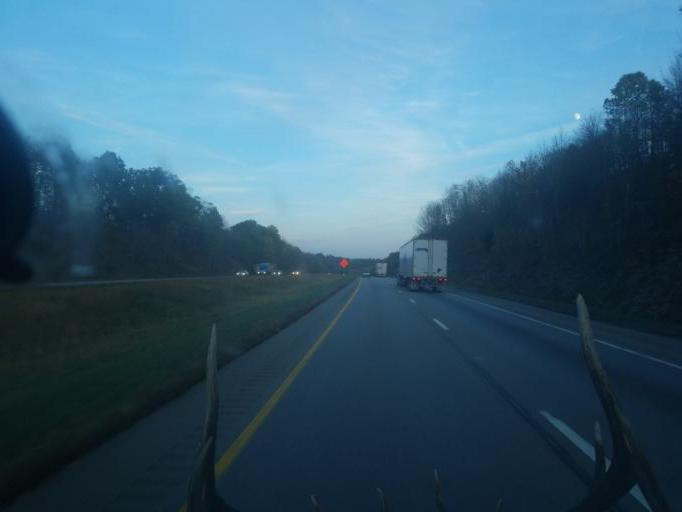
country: US
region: Ohio
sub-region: Muskingum County
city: New Concord
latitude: 39.9711
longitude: -81.8148
